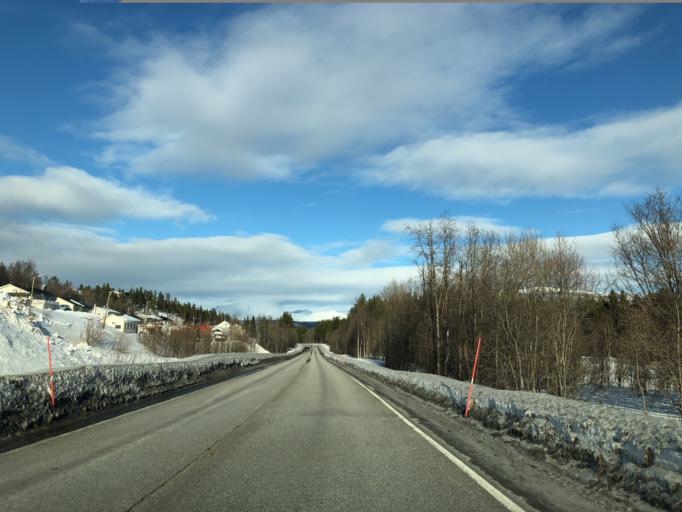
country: NO
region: Troms
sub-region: Malselv
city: Moen
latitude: 69.0830
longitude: 18.5743
